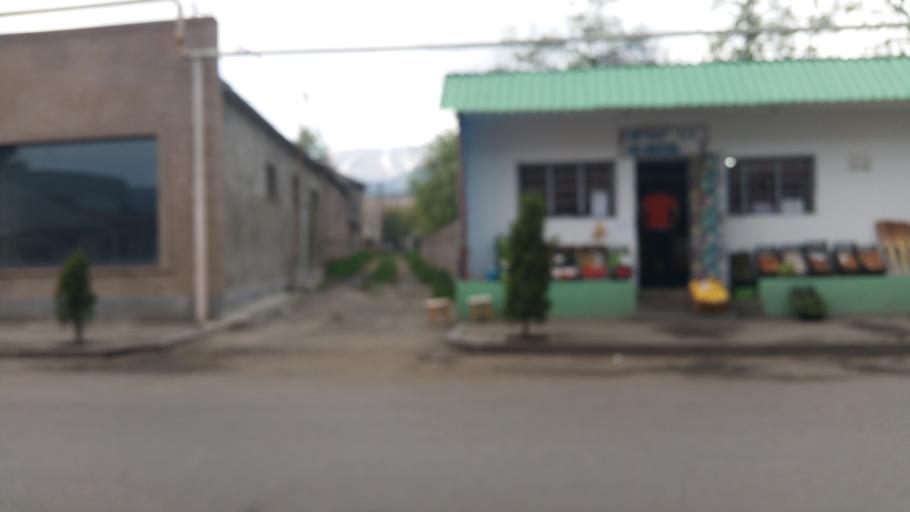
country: AM
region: Lorri
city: Urrut
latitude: 41.0090
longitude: 44.3904
